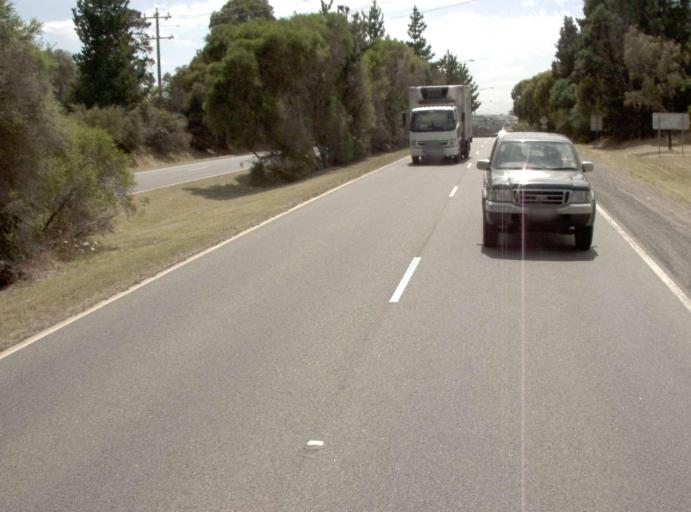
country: AU
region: Victoria
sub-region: Cardinia
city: Pakenham Upper
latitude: -38.0697
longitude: 145.4945
